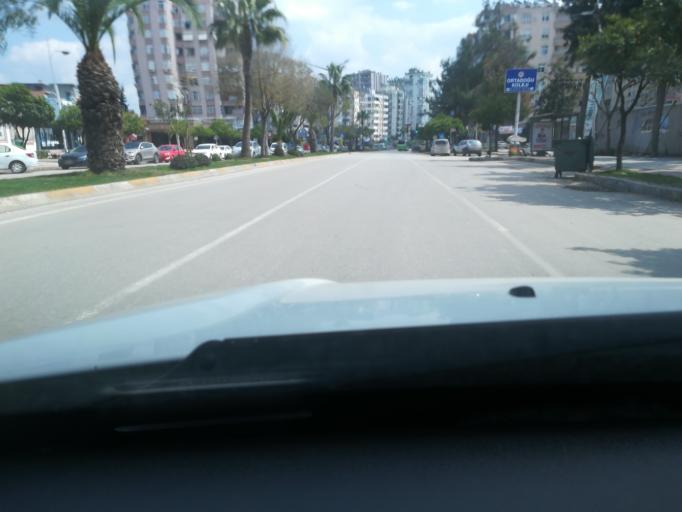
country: TR
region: Adana
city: Adana
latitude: 37.0459
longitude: 35.3064
